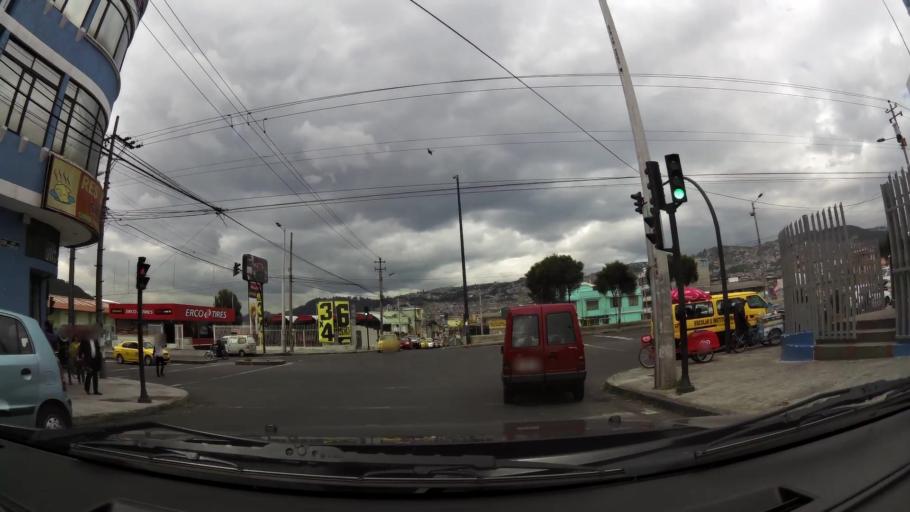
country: EC
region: Pichincha
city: Quito
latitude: -0.2461
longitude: -78.5310
